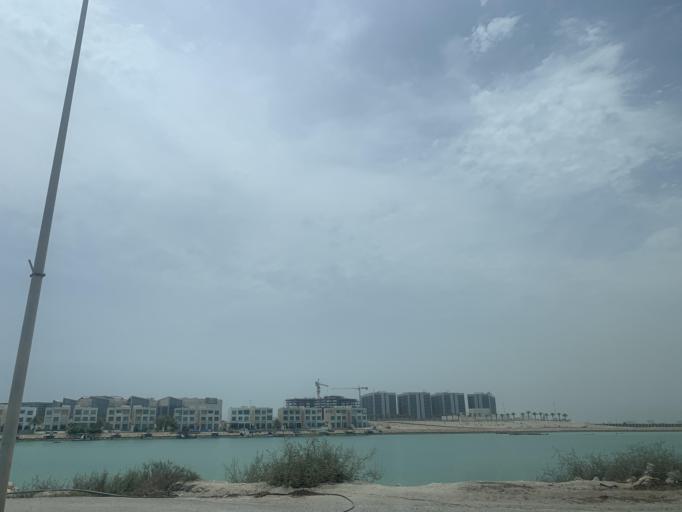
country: BH
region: Muharraq
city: Al Hadd
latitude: 26.2757
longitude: 50.6678
